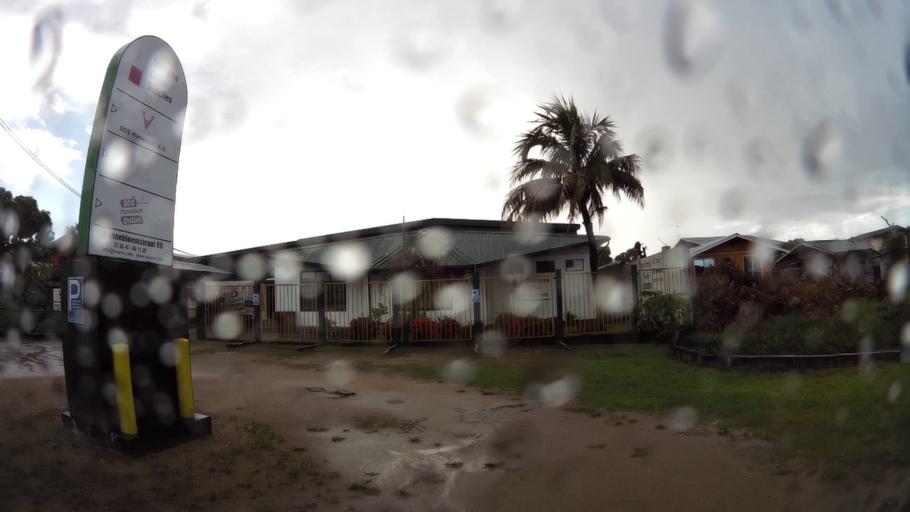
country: SR
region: Paramaribo
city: Paramaribo
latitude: 5.8192
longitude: -55.1865
